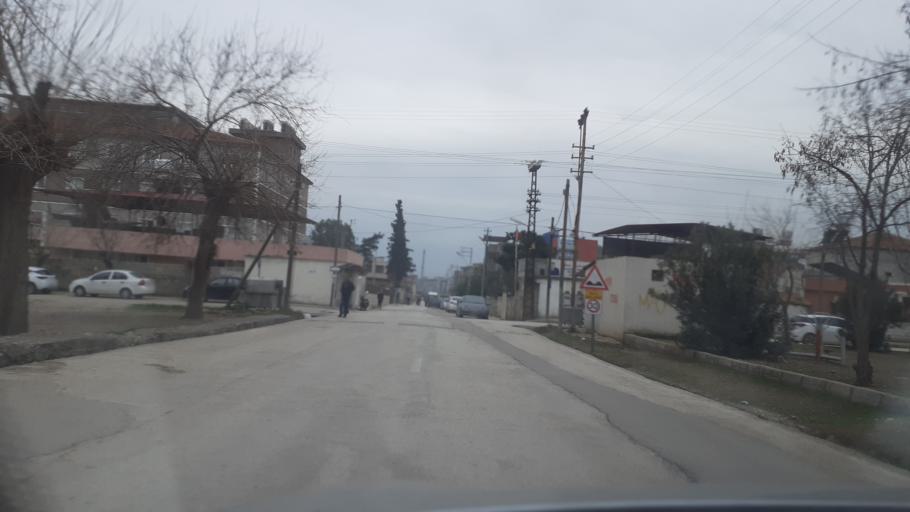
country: TR
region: Hatay
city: Kirikhan
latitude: 36.4884
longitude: 36.3557
